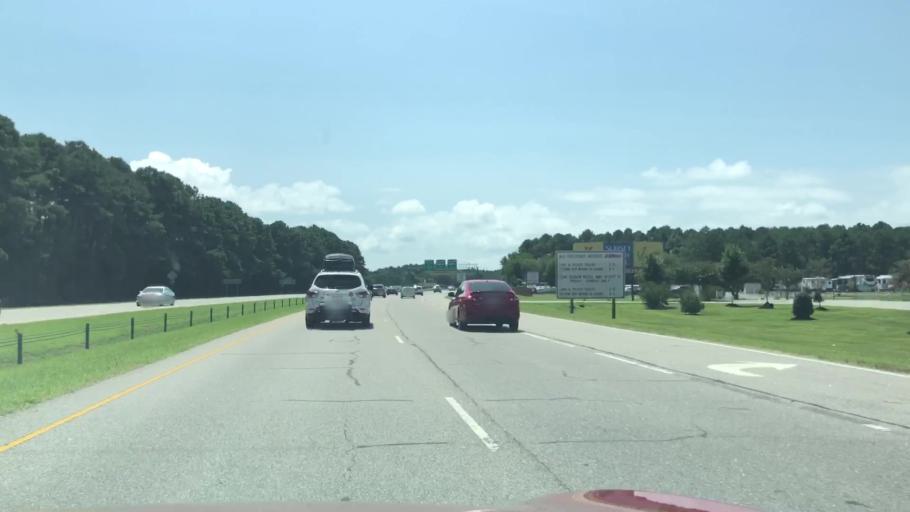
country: US
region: Virginia
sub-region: Northampton County
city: Cape Charles
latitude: 37.1376
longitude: -75.9666
